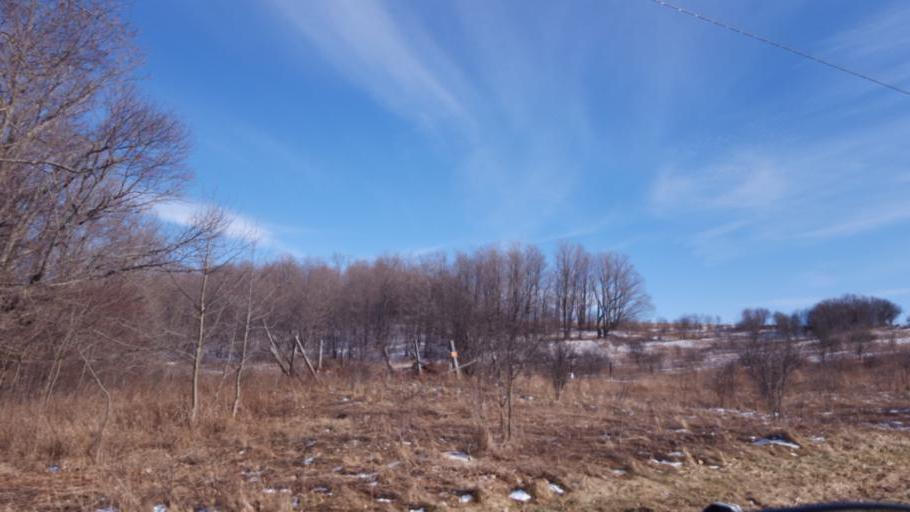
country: US
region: New York
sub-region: Allegany County
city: Wellsville
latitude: 42.1029
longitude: -77.9955
